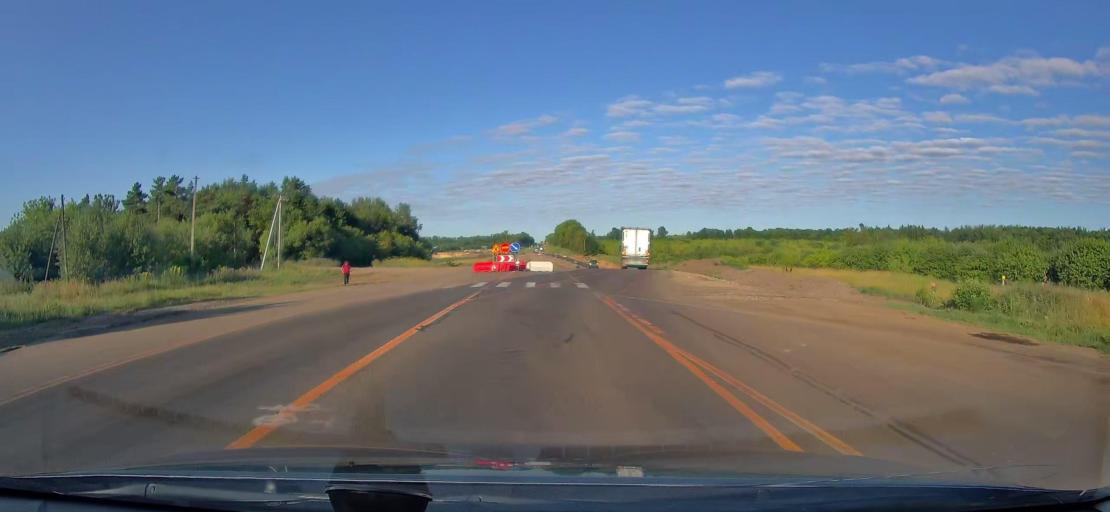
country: RU
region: Tula
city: Bol'shoye Skuratovo
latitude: 53.4452
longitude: 36.8386
